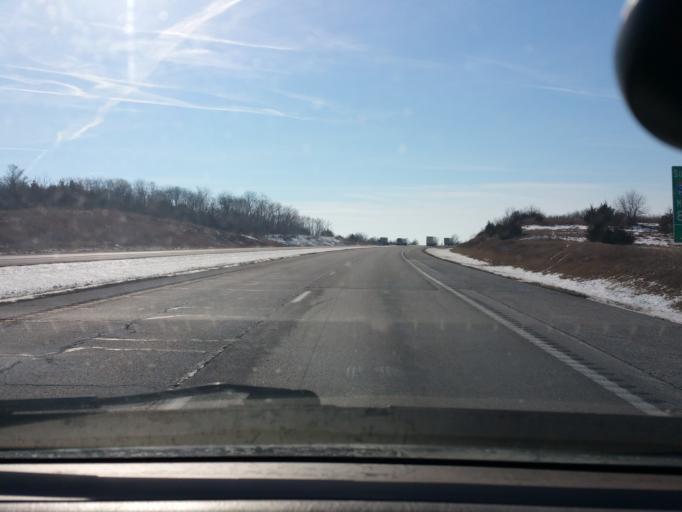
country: US
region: Missouri
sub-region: Harrison County
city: Bethany
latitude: 40.1811
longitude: -94.0154
